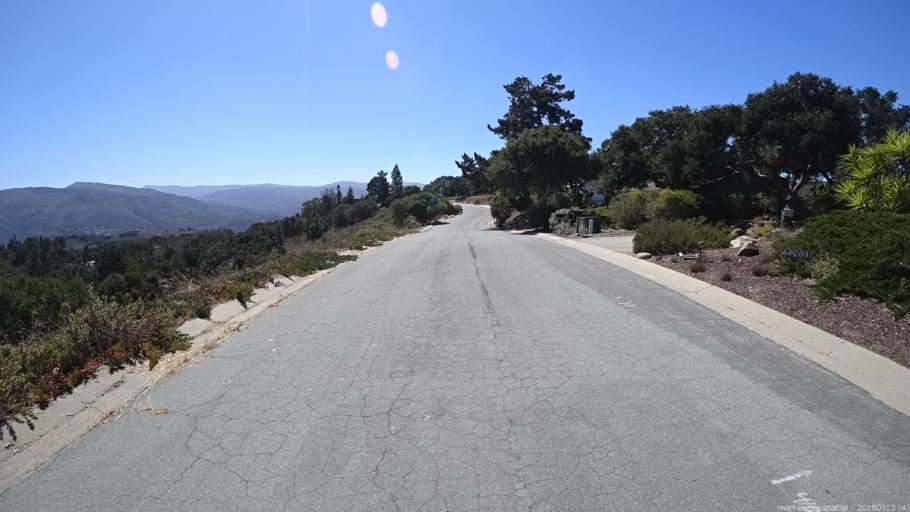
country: US
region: California
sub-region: Monterey County
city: Carmel Valley Village
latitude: 36.5402
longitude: -121.7986
